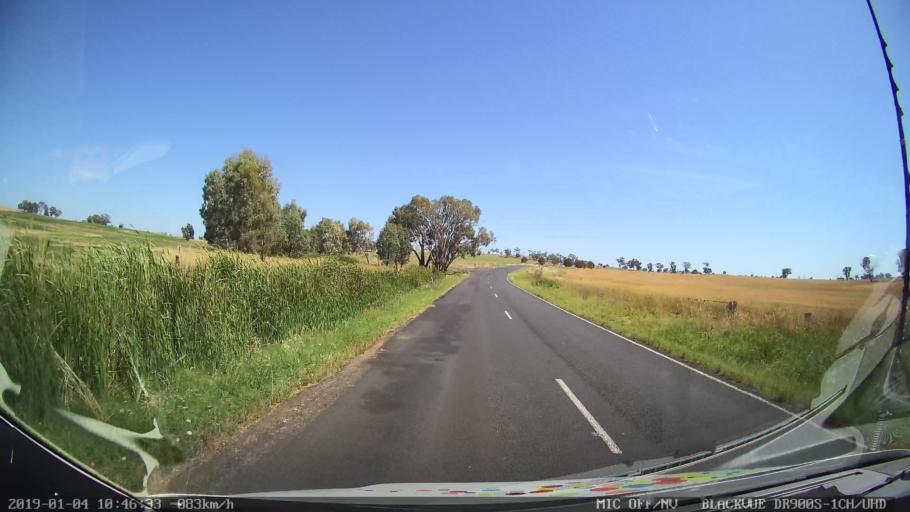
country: AU
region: New South Wales
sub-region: Cabonne
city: Molong
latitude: -33.2801
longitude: 148.7222
